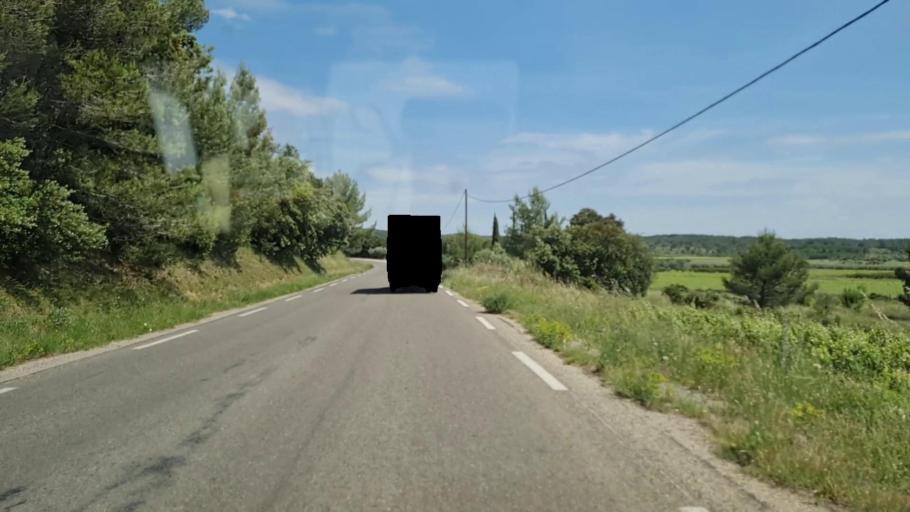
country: FR
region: Languedoc-Roussillon
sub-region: Departement du Gard
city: Cabrieres
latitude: 43.8907
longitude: 4.4728
